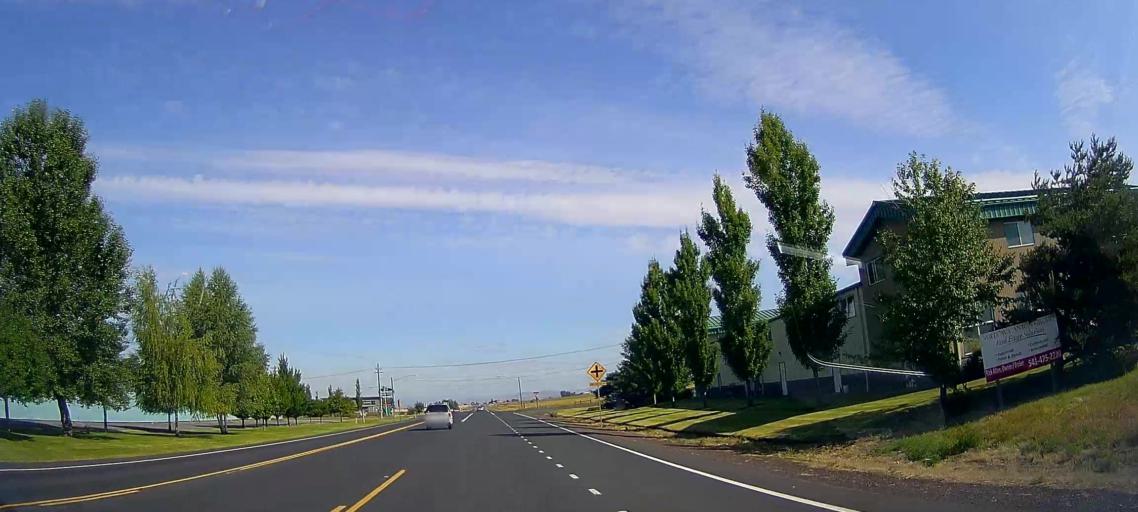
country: US
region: Oregon
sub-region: Jefferson County
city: Madras
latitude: 44.6636
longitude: -121.1351
